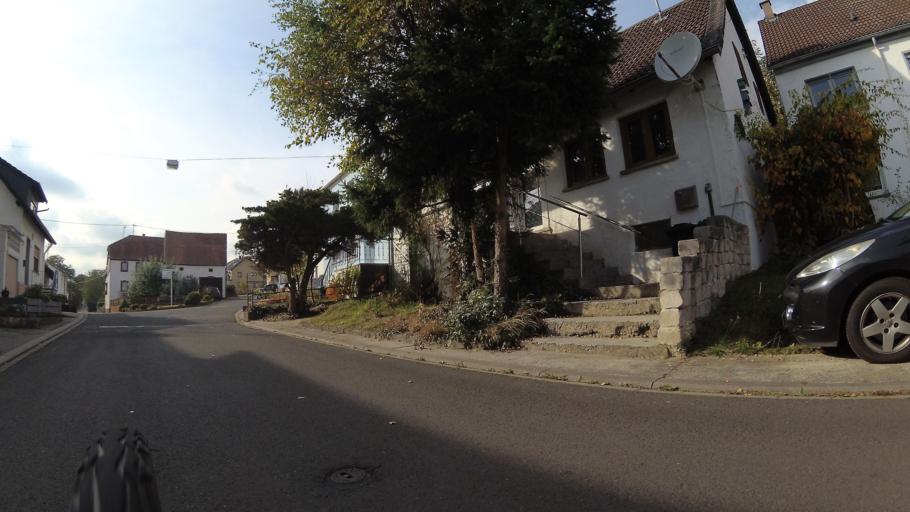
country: DE
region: Rheinland-Pfalz
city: Pfeffelbach
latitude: 49.5377
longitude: 7.3278
